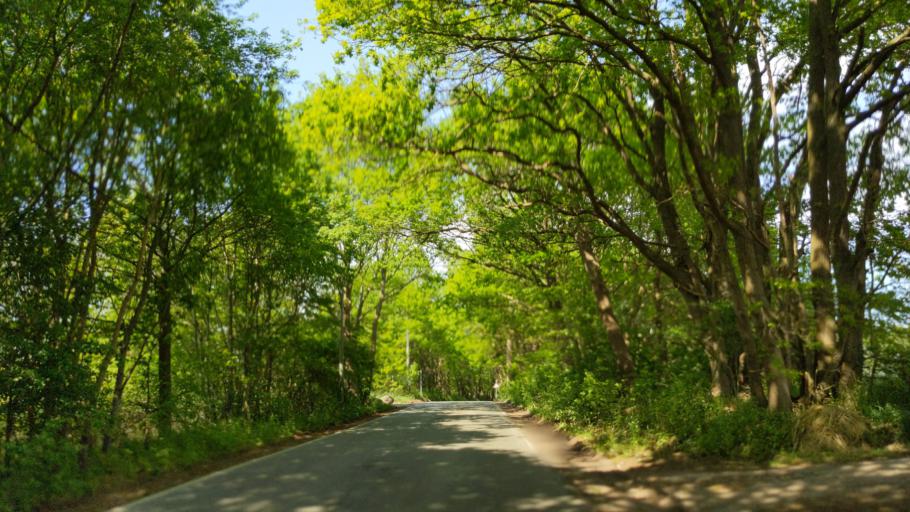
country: DE
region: Mecklenburg-Vorpommern
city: Selmsdorf
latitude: 53.8817
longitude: 10.8208
